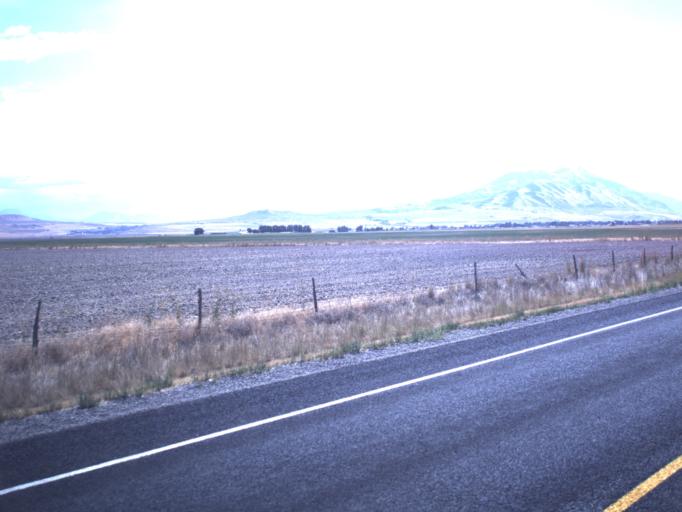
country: US
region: Utah
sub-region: Box Elder County
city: Garland
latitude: 41.8590
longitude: -112.1466
